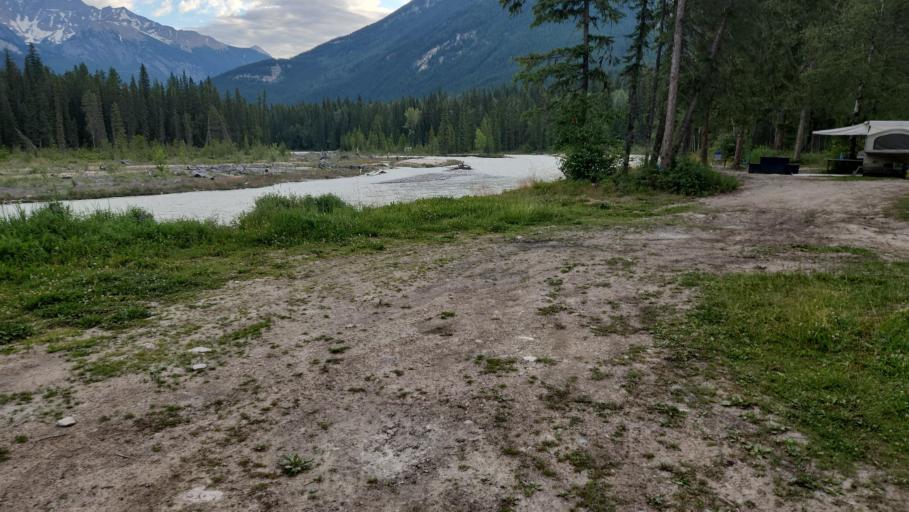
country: CA
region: British Columbia
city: Golden
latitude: 51.4758
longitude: -116.9726
